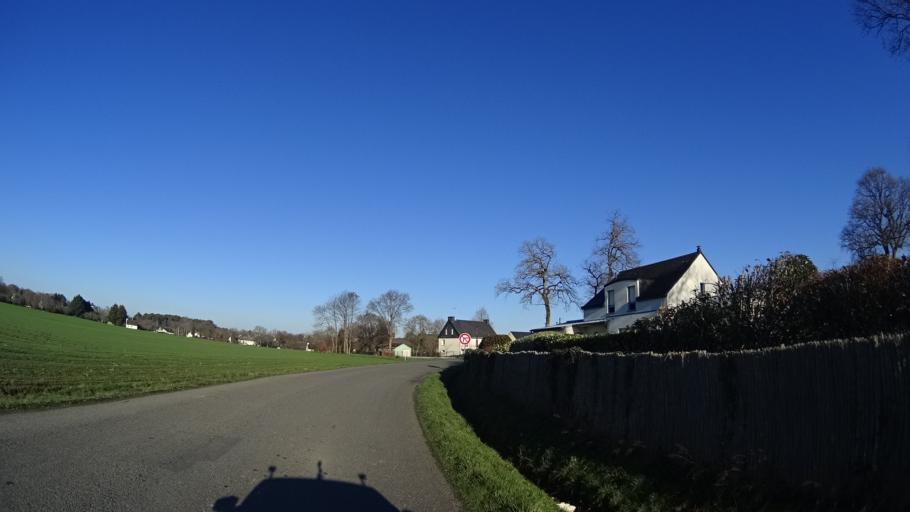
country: FR
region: Brittany
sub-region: Departement du Morbihan
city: Allaire
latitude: 47.6382
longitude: -2.1752
